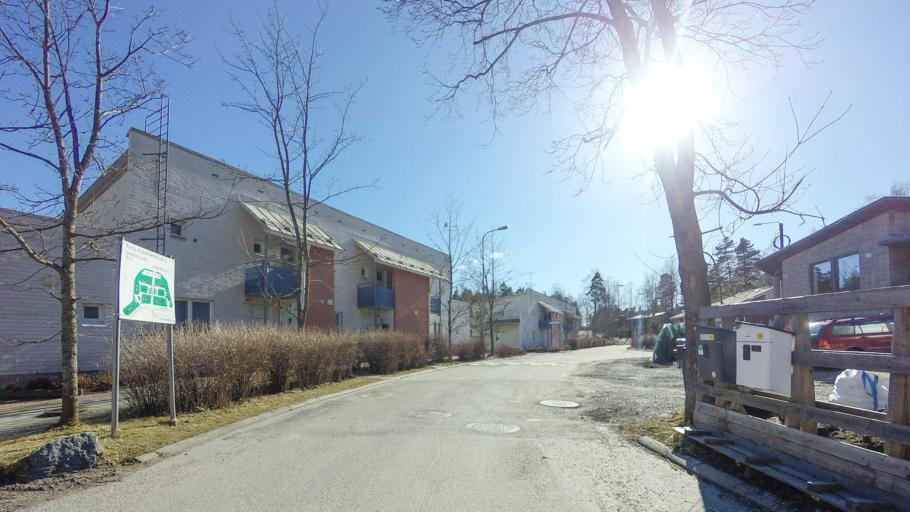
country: FI
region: Uusimaa
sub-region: Helsinki
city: Helsinki
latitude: 60.1607
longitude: 25.0716
